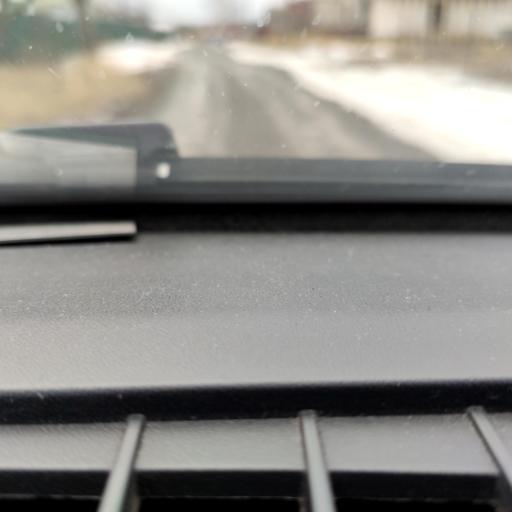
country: RU
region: Voronezj
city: Devitsa
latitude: 51.6357
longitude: 38.9269
